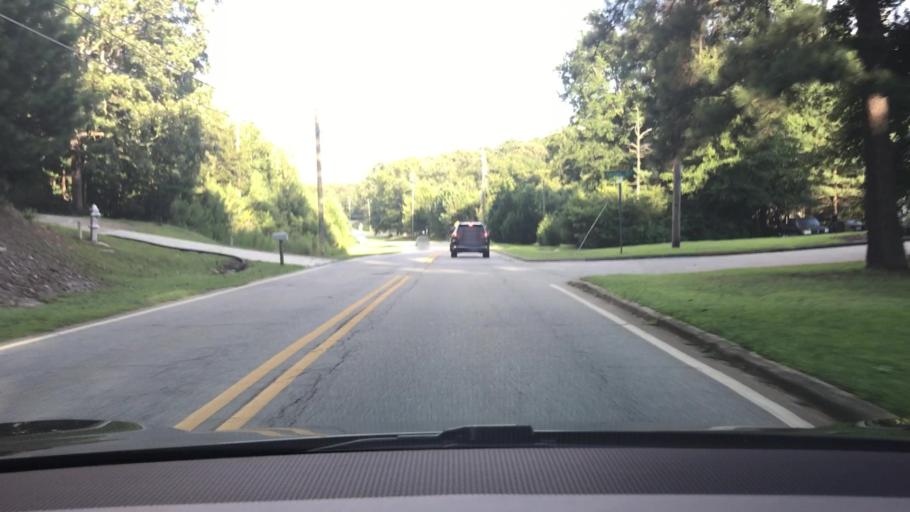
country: US
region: Georgia
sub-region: Gwinnett County
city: Sugar Hill
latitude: 34.0830
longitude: -84.0412
